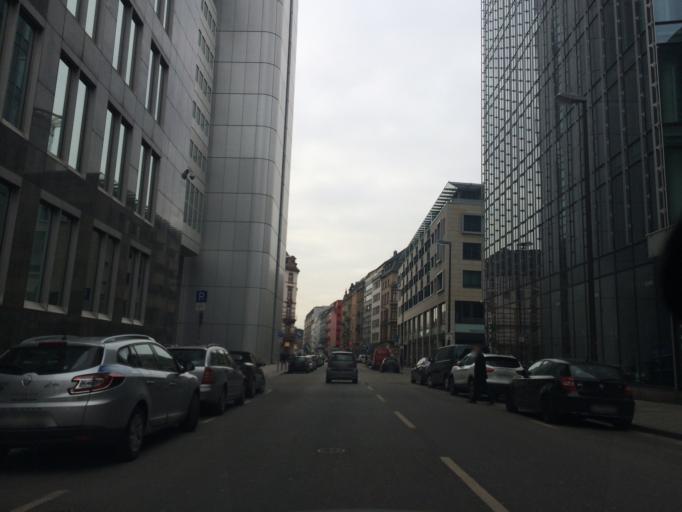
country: DE
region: Hesse
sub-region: Regierungsbezirk Darmstadt
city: Frankfurt am Main
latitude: 50.1102
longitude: 8.6700
